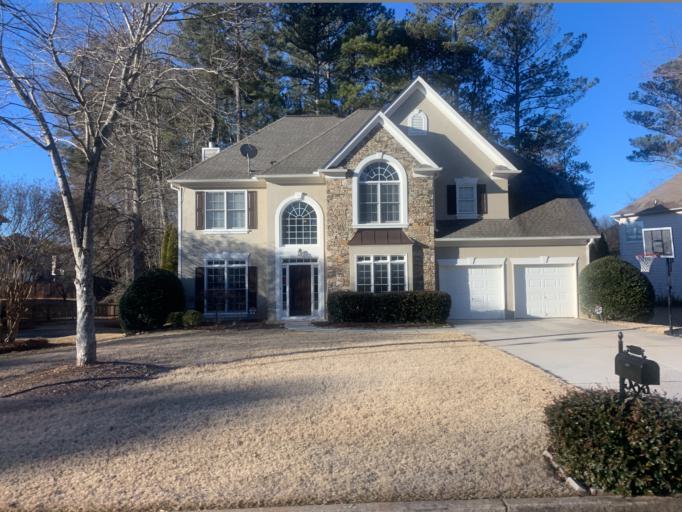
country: US
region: Georgia
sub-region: Gwinnett County
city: Mountain Park
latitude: 33.8638
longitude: -84.1082
